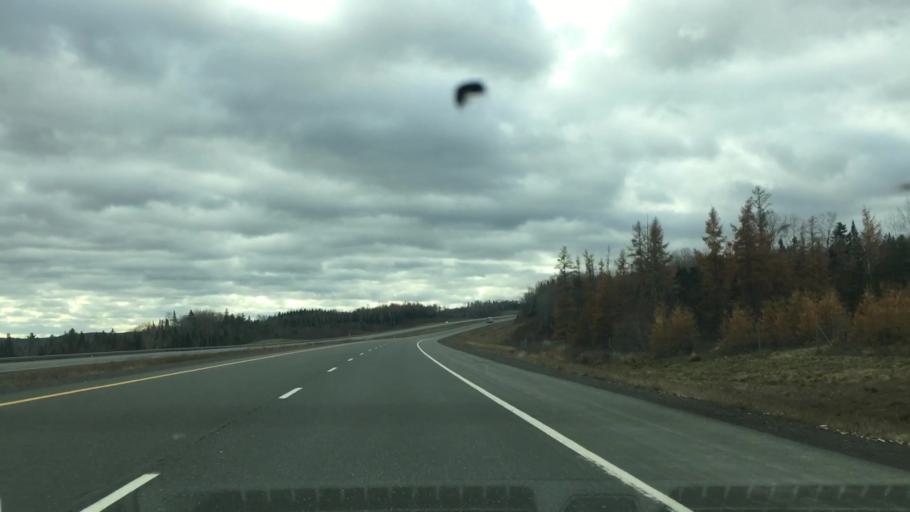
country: US
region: Maine
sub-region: Aroostook County
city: Fort Fairfield
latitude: 46.6702
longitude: -67.7302
